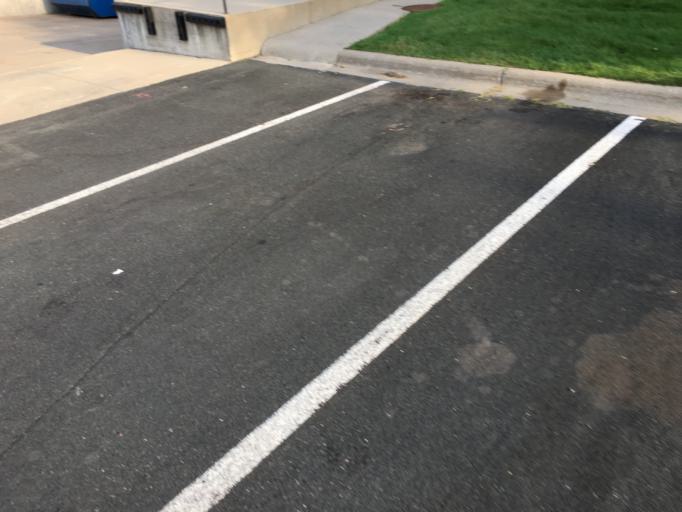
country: US
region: Minnesota
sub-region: Stearns County
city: Saint Cloud
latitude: 45.5535
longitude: -94.1540
